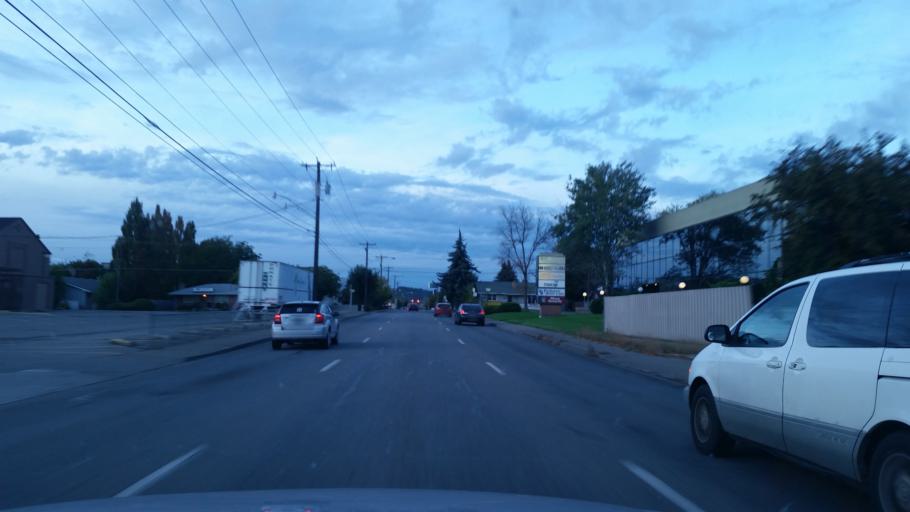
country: US
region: Washington
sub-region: Spokane County
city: Dishman
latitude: 47.6669
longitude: -117.2816
